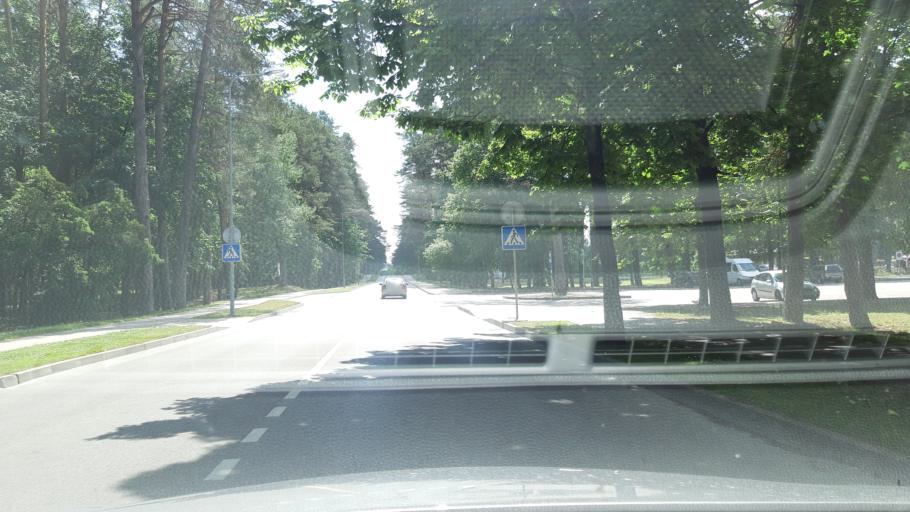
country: LT
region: Alytaus apskritis
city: Druskininkai
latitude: 54.0104
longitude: 23.9776
